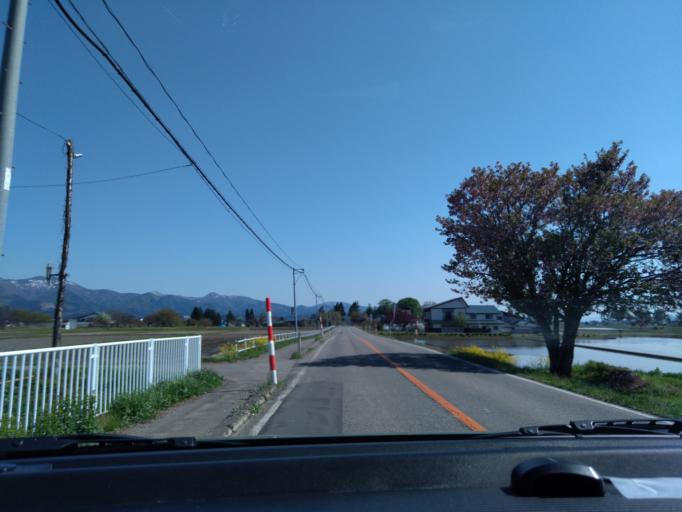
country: JP
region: Akita
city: Kakunodatemachi
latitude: 39.5270
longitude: 140.5868
